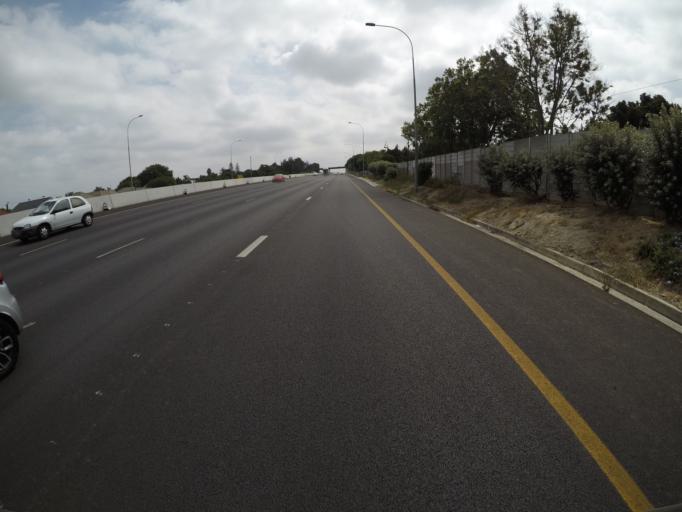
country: ZA
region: Western Cape
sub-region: City of Cape Town
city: Kraaifontein
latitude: -33.8884
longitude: 18.6226
